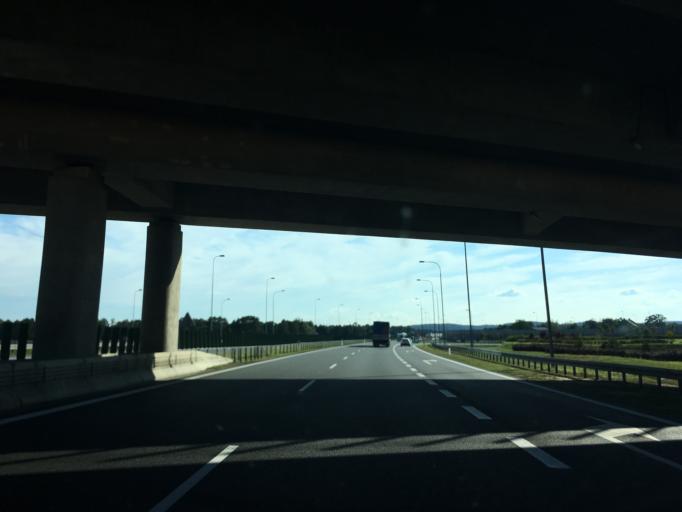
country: PL
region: Kujawsko-Pomorskie
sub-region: Grudziadz
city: Grudziadz
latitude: 53.4276
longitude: 18.6932
